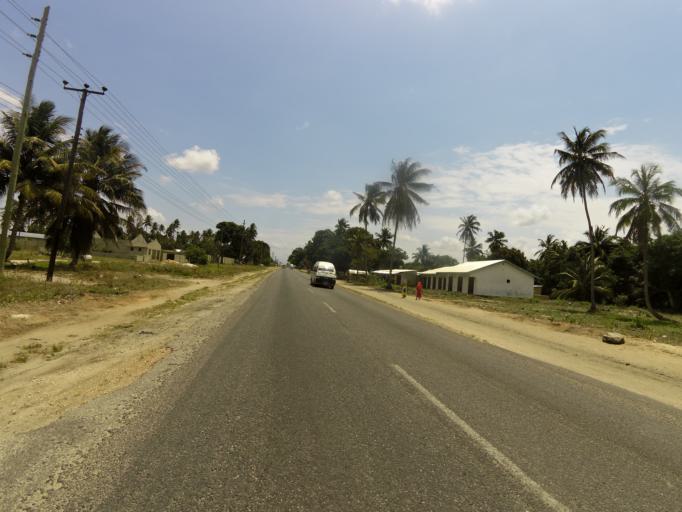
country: TZ
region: Pwani
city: Vikindu
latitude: -7.0331
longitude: 39.2851
